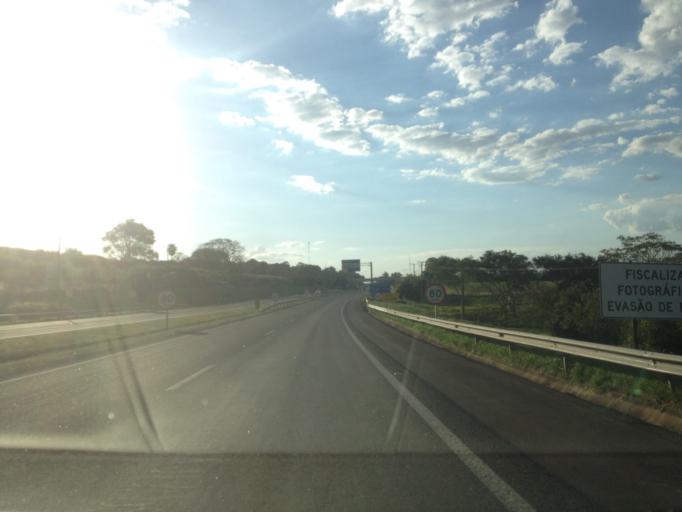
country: BR
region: Sao Paulo
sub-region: Brotas
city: Brotas
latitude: -22.2596
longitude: -48.2404
